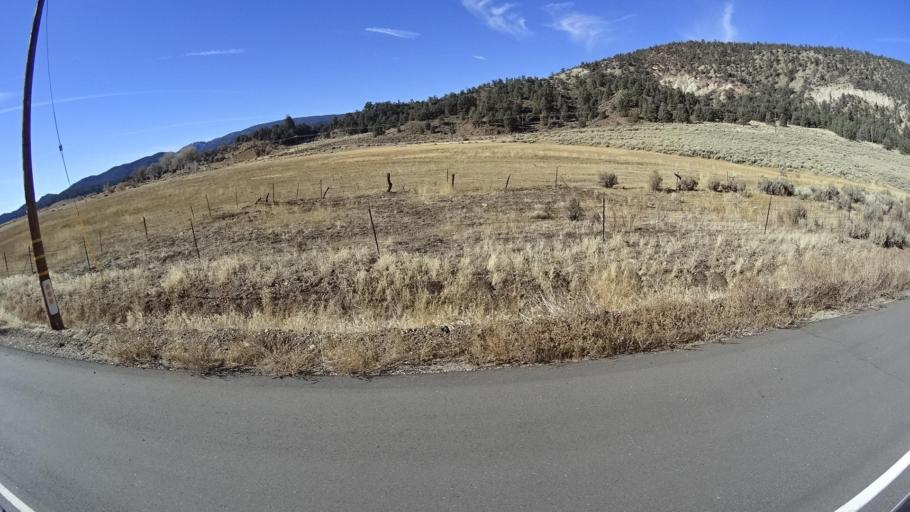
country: US
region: California
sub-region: Kern County
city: Frazier Park
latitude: 34.8106
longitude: -119.0114
